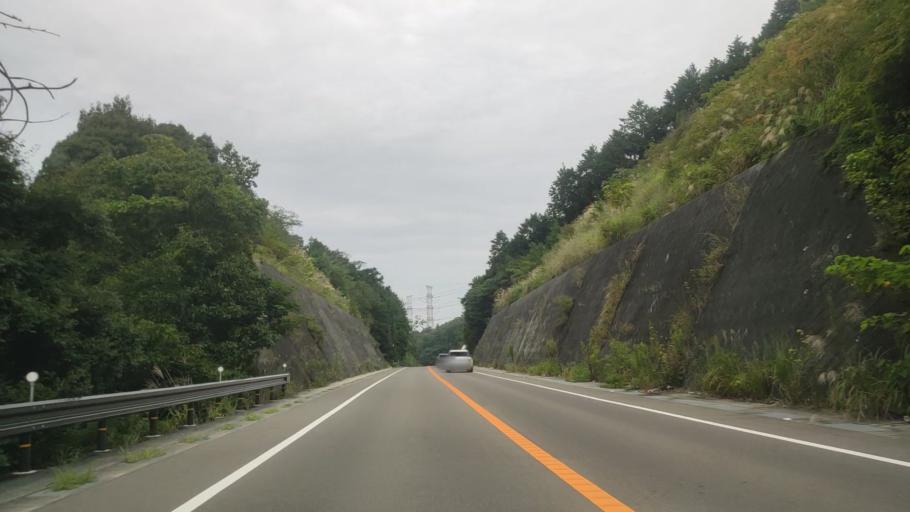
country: JP
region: Wakayama
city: Hashimoto
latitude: 34.3997
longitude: 135.5955
